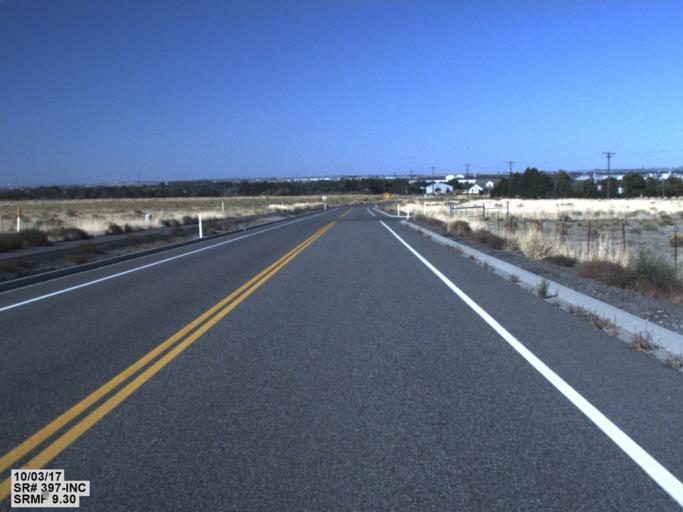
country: US
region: Washington
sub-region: Benton County
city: Finley
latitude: 46.1341
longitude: -119.0350
